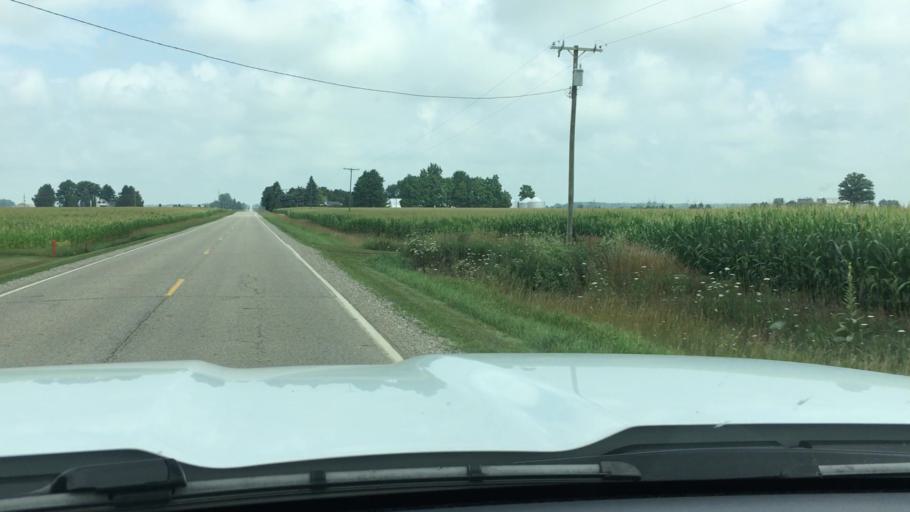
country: US
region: Michigan
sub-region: Sanilac County
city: Marlette
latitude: 43.3819
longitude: -83.0067
